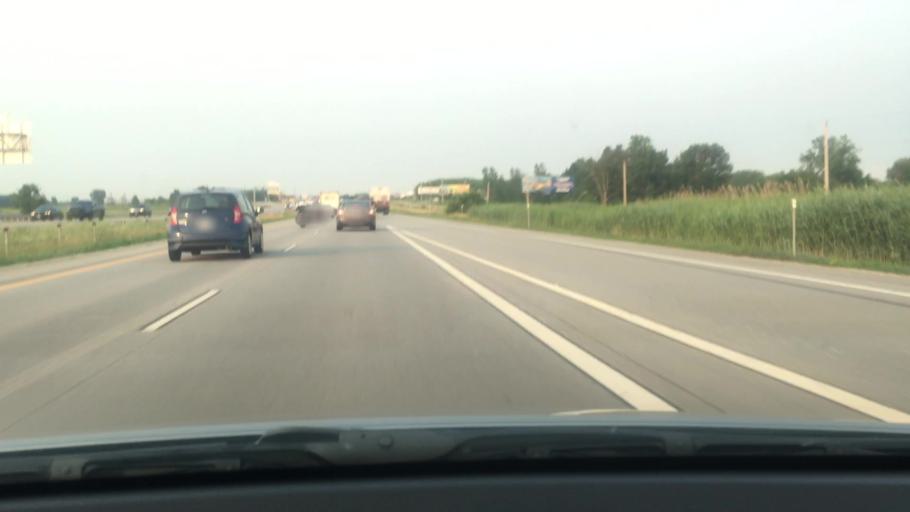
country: US
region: Wisconsin
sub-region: Brown County
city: Wrightstown
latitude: 44.3464
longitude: -88.1963
